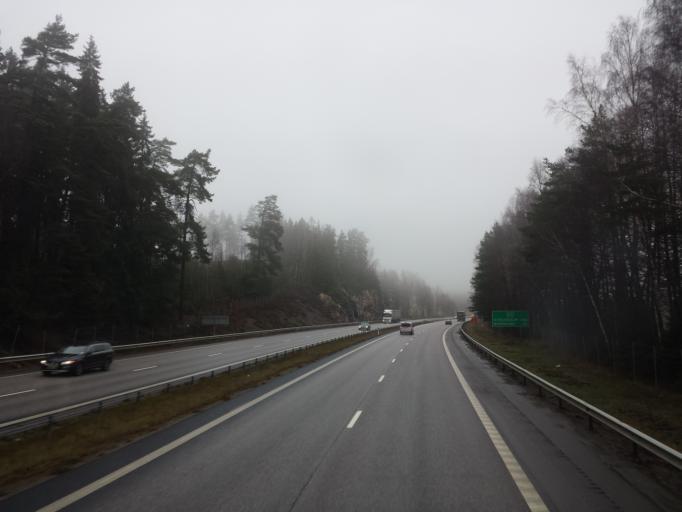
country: SE
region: OEstergoetland
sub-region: Norrkopings Kommun
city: Krokek
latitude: 58.6971
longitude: 16.3375
